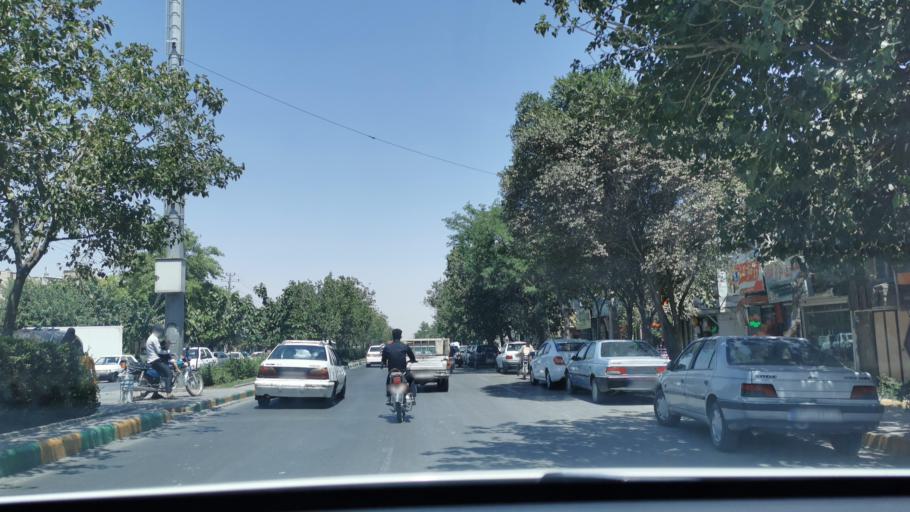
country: IR
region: Razavi Khorasan
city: Mashhad
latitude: 36.3431
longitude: 59.6257
